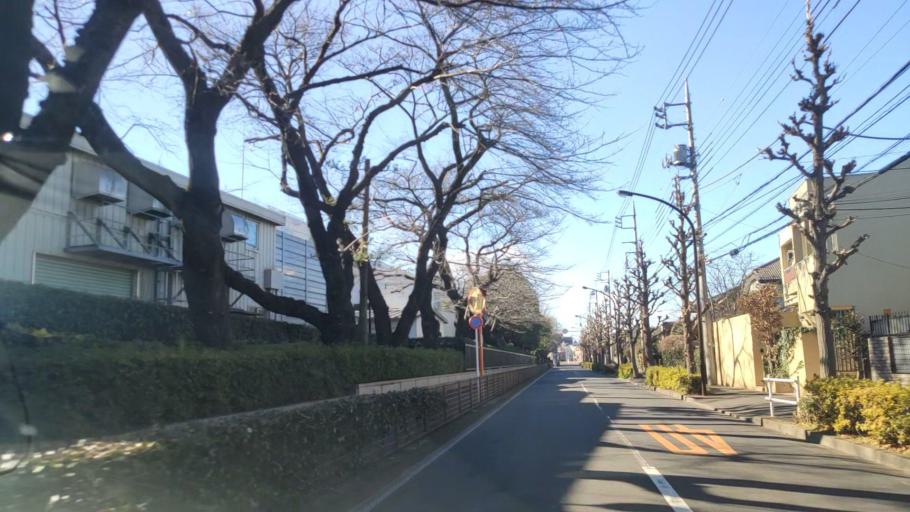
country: JP
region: Tokyo
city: Musashino
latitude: 35.7209
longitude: 139.5640
